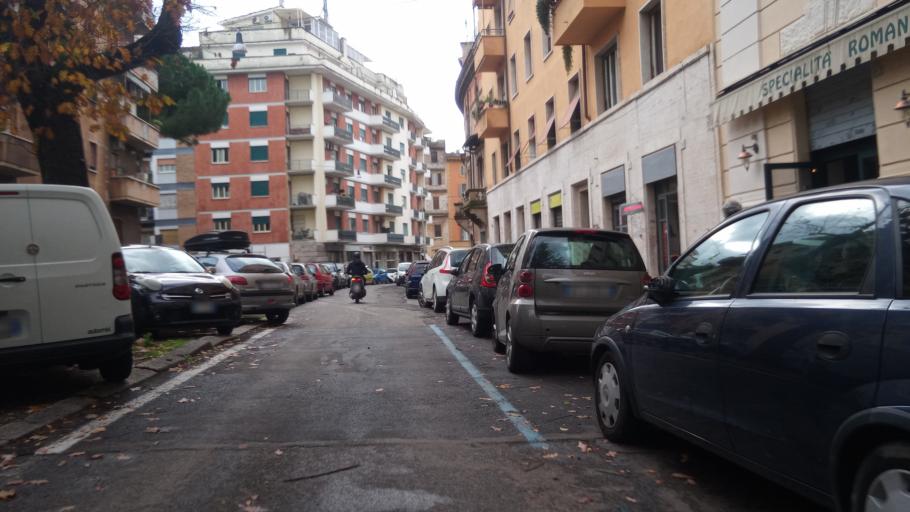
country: IT
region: Latium
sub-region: Citta metropolitana di Roma Capitale
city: Rome
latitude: 41.8986
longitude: 12.5110
